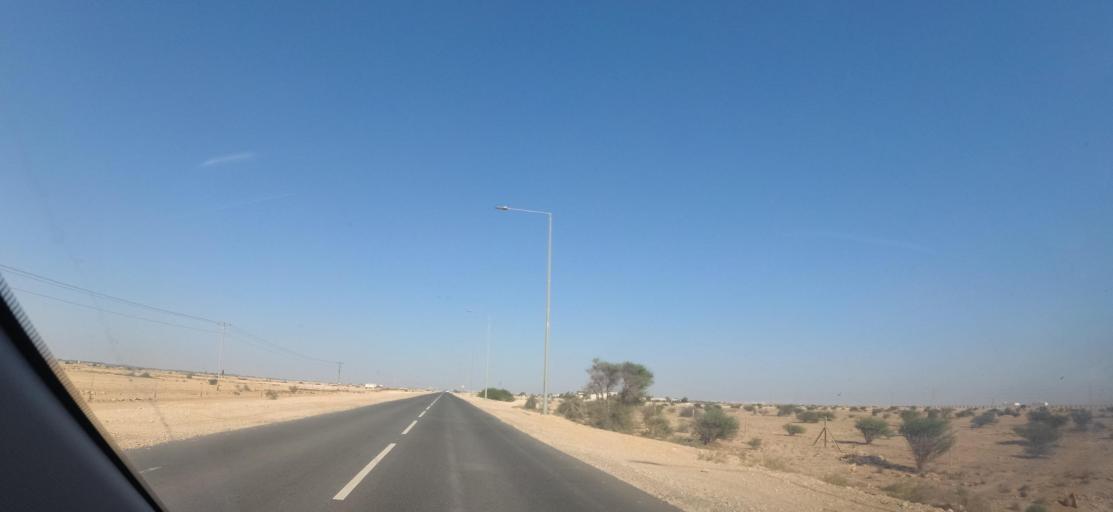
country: QA
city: Al Ghuwayriyah
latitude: 25.8417
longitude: 51.2621
